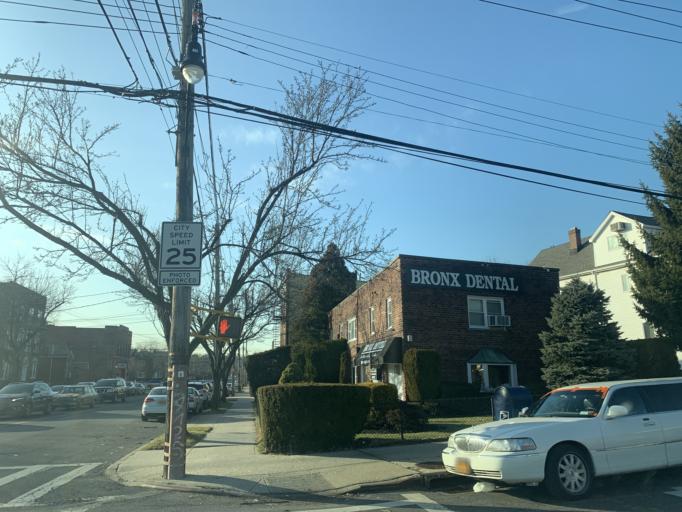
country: US
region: New York
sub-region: Bronx
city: The Bronx
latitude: 40.8596
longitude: -73.8430
